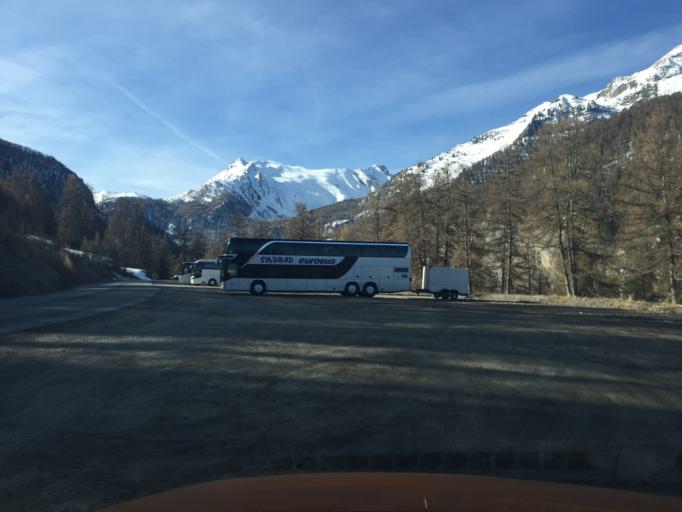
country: FR
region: Provence-Alpes-Cote d'Azur
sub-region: Departement des Hautes-Alpes
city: Embrun
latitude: 44.4863
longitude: 6.5503
